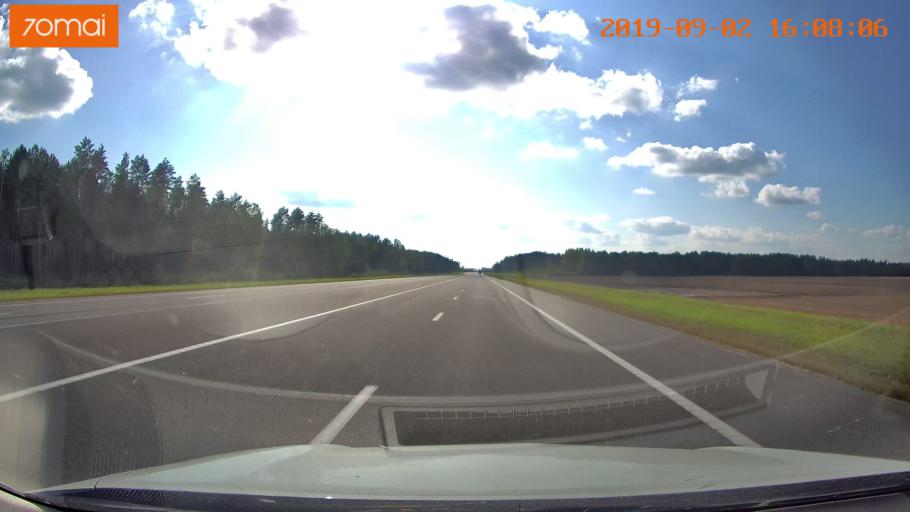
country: BY
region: Minsk
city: Byerazino
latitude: 53.7774
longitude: 28.7383
